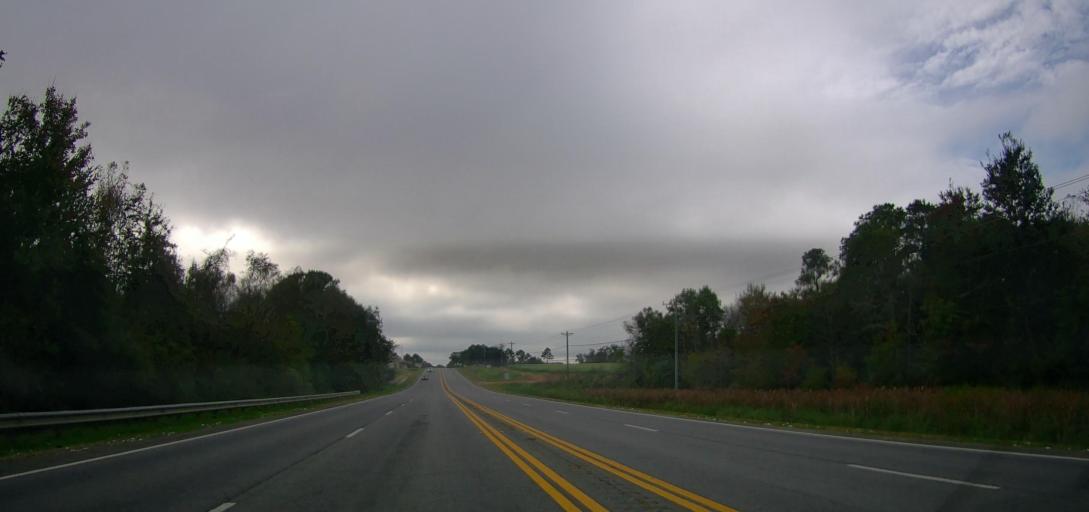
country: US
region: Georgia
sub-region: Tift County
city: Omega
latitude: 31.3506
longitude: -83.5856
